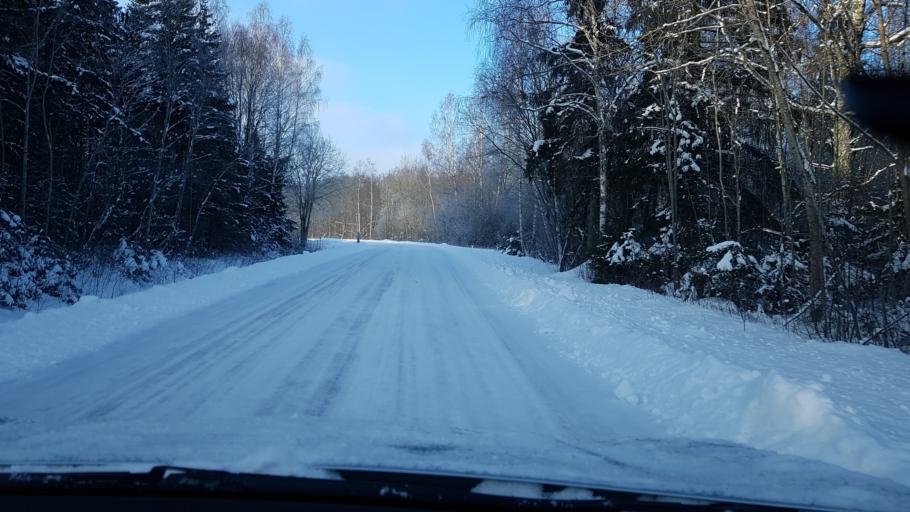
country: EE
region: Harju
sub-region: Nissi vald
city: Turba
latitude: 59.1042
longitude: 24.2423
